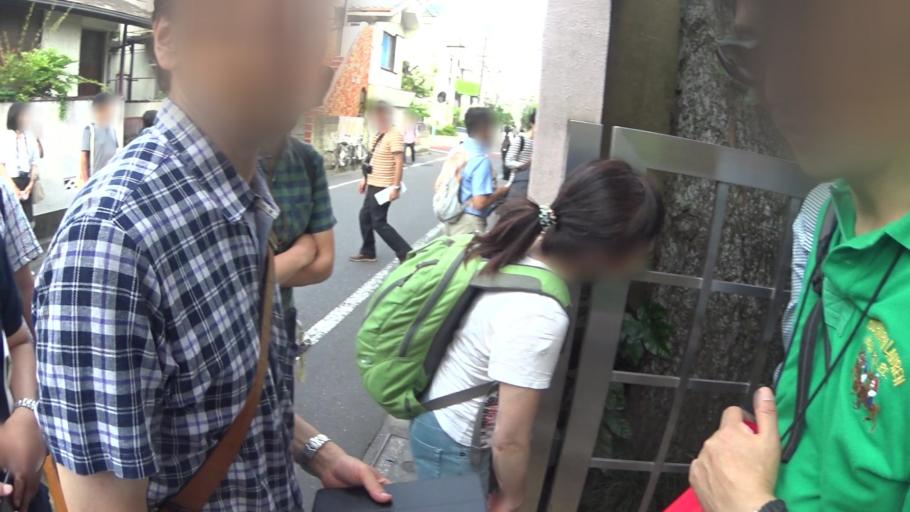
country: JP
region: Tokyo
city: Musashino
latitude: 35.7030
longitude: 139.6255
